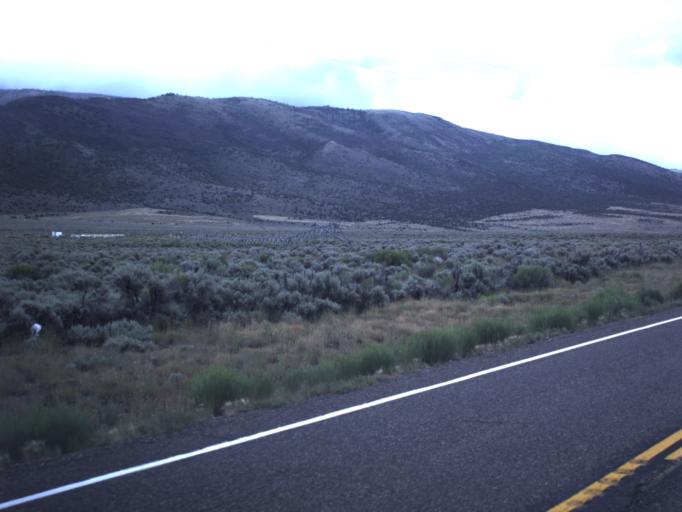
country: US
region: Utah
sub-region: Wayne County
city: Loa
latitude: 38.5817
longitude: -111.8438
